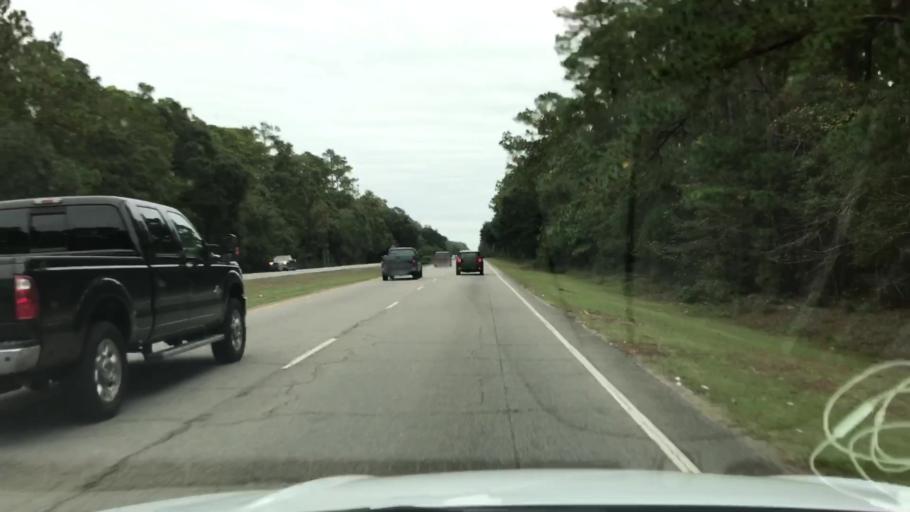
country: US
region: South Carolina
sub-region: Georgetown County
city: Murrells Inlet
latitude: 33.5000
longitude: -79.0831
